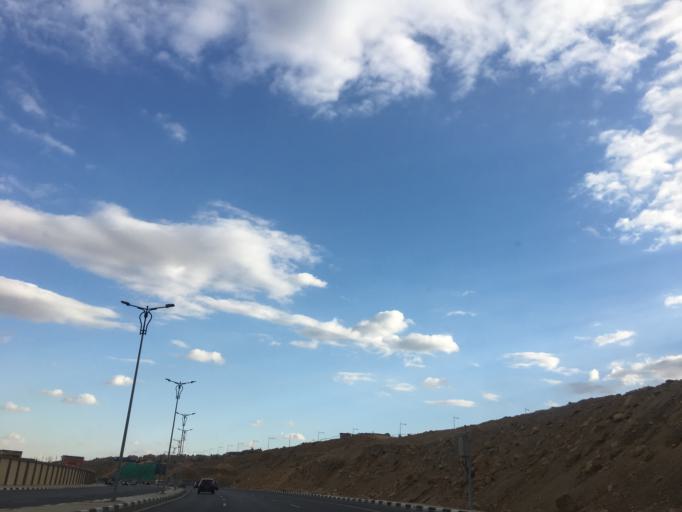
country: EG
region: Muhafazat al Qahirah
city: Cairo
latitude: 30.0299
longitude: 31.3097
